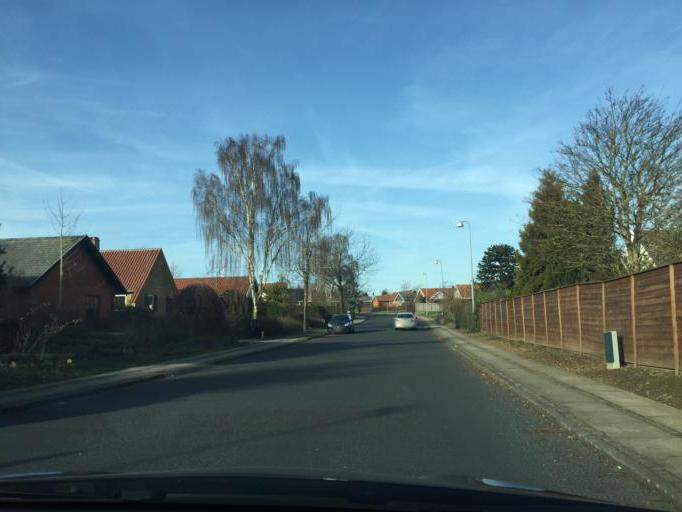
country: DK
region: South Denmark
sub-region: Odense Kommune
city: Odense
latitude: 55.3686
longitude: 10.3550
